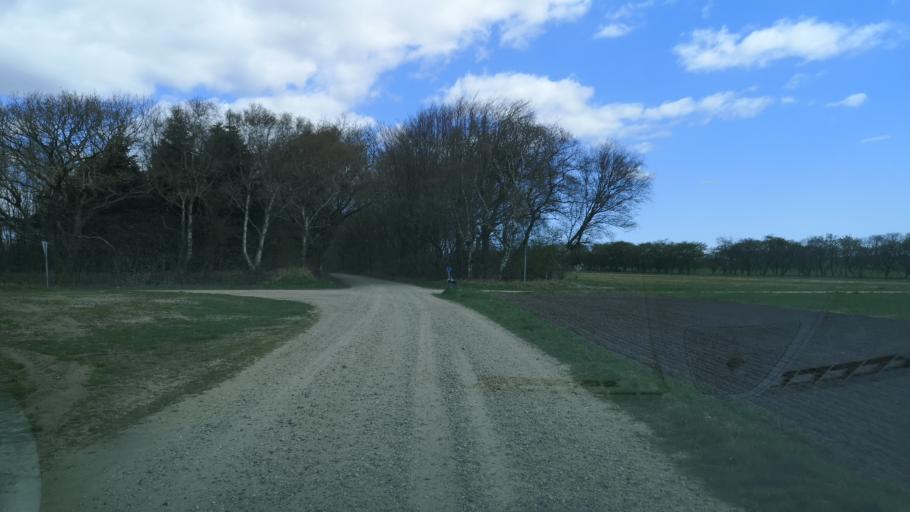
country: DK
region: Central Jutland
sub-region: Ringkobing-Skjern Kommune
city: Skjern
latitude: 55.9749
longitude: 8.5054
